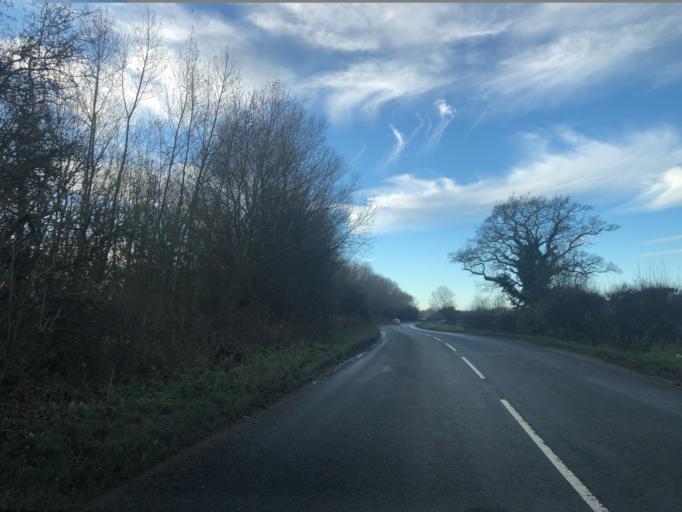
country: GB
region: England
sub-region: North Yorkshire
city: Thirsk
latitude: 54.1818
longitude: -1.3604
